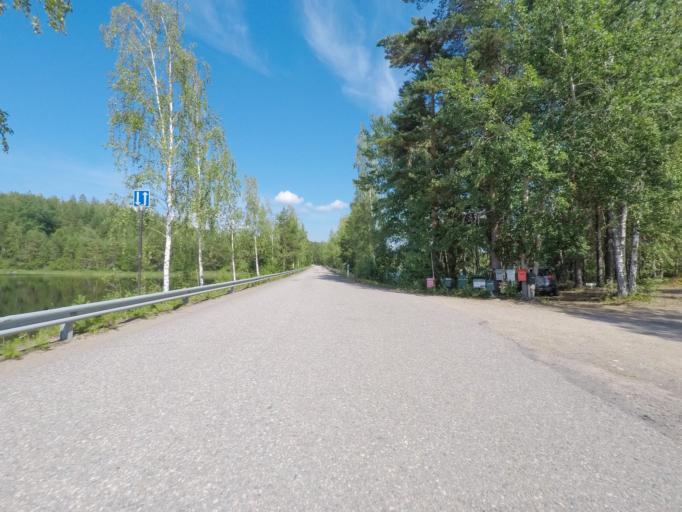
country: FI
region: Southern Savonia
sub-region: Mikkeli
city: Puumala
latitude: 61.4086
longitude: 28.0894
